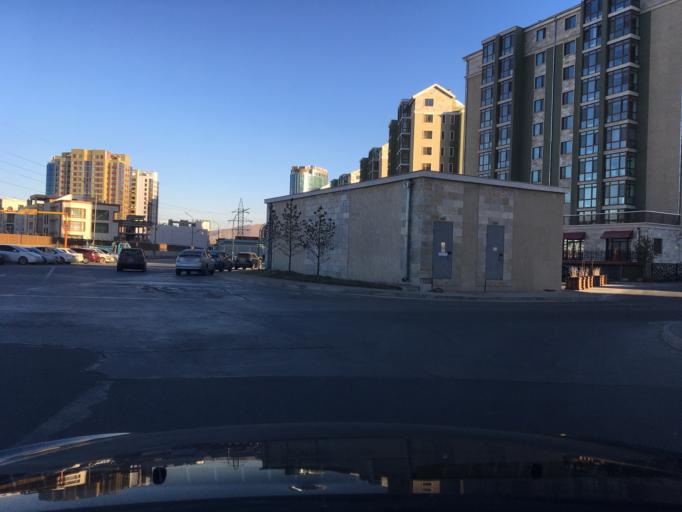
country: MN
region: Ulaanbaatar
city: Ulaanbaatar
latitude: 47.8910
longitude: 106.9283
